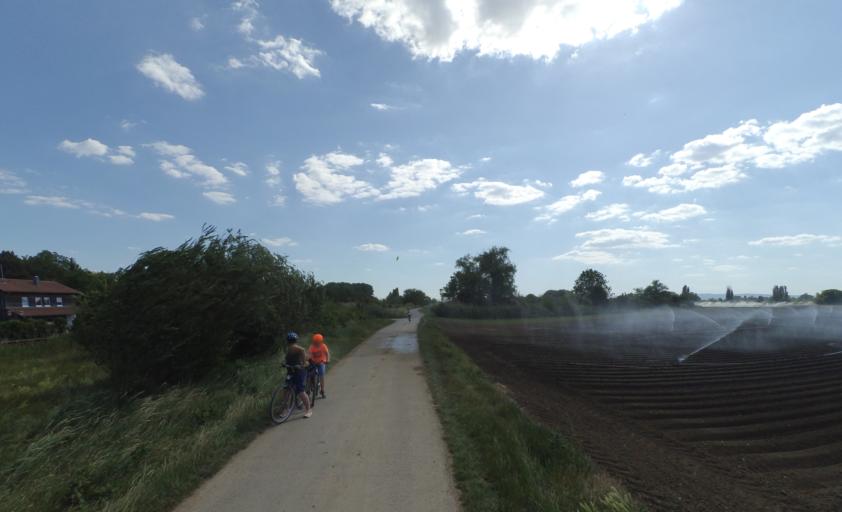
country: DE
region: Rheinland-Pfalz
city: Frankenthal
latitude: 49.5175
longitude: 8.3791
